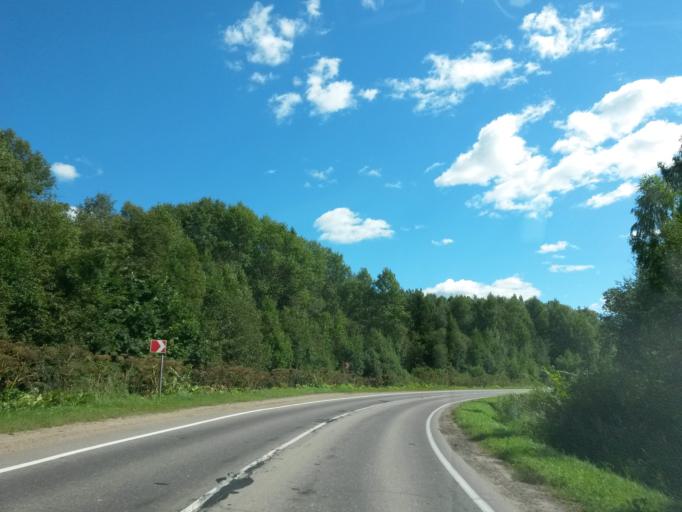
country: RU
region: Jaroslavl
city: Yaroslavl
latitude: 57.8012
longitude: 39.8258
